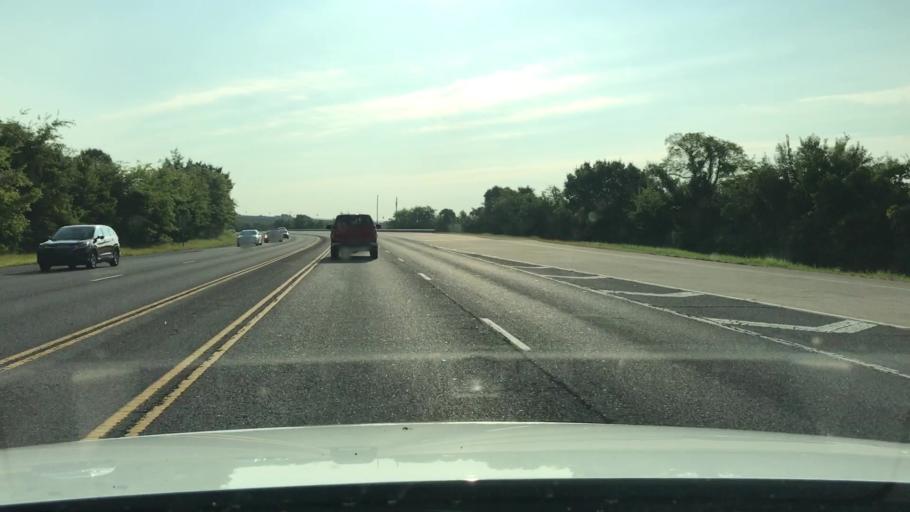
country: US
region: Tennessee
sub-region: Sumner County
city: Hendersonville
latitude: 36.3298
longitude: -86.5546
